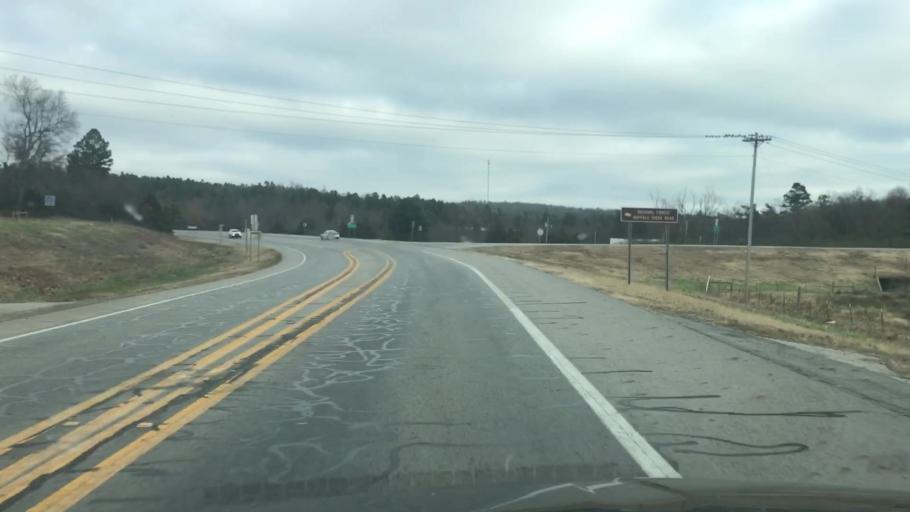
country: US
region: Arkansas
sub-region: Scott County
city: Waldron
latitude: 34.8076
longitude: -94.0396
